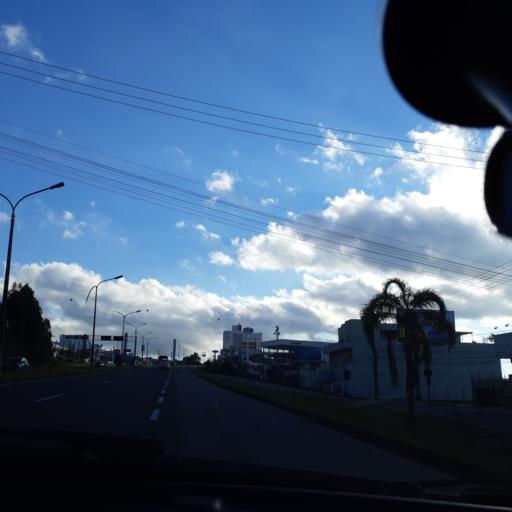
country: BR
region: Rio Grande do Sul
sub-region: Caxias Do Sul
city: Caxias do Sul
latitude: -29.1751
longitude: -51.2105
